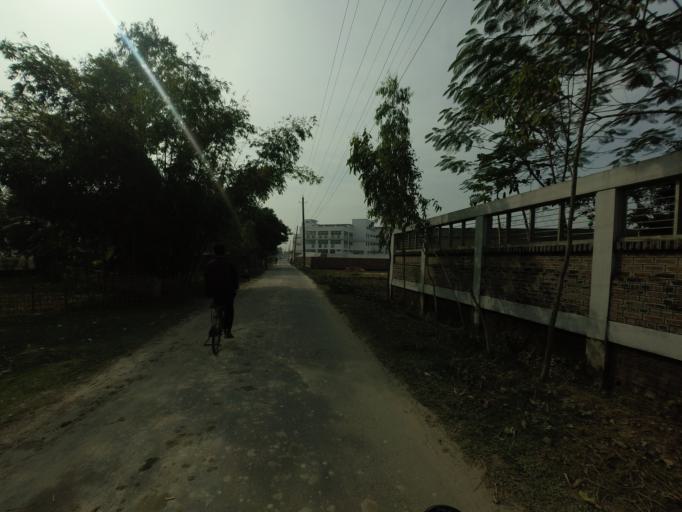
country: BD
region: Rajshahi
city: Saidpur
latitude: 25.9236
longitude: 88.8382
